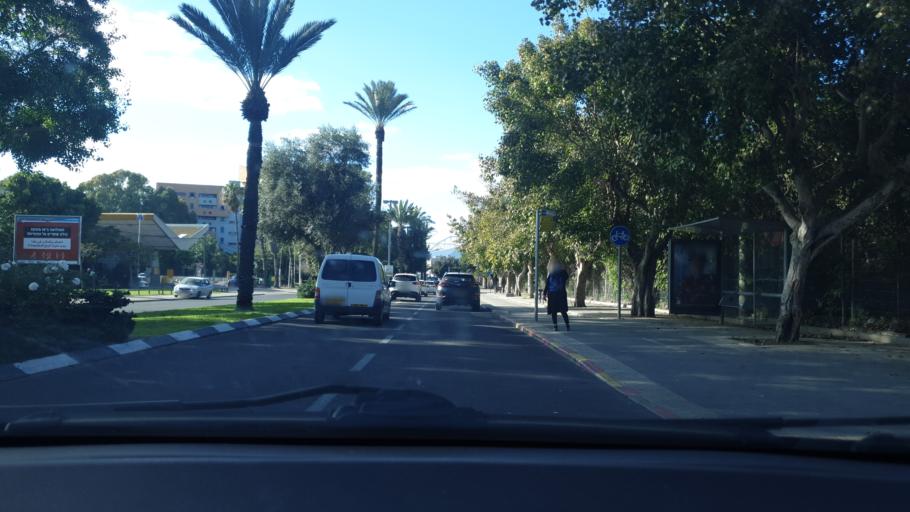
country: IL
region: Tel Aviv
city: Yafo
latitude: 32.0461
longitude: 34.7672
